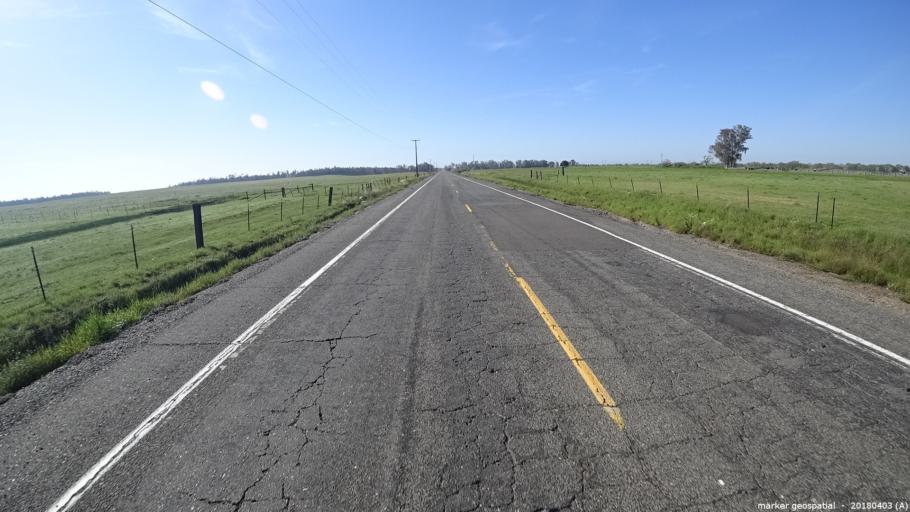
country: US
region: California
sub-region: Sacramento County
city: Clay
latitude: 38.3656
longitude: -121.1684
